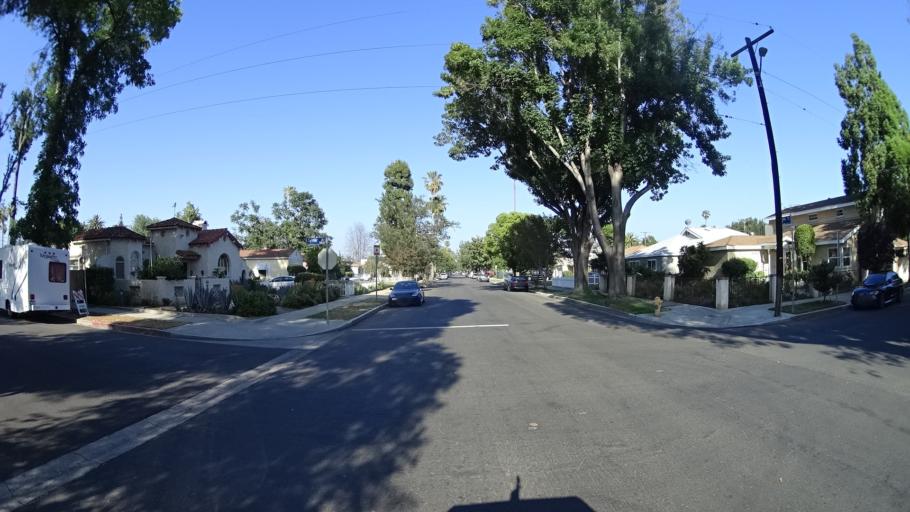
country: US
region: California
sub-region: Los Angeles County
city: Van Nuys
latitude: 34.1767
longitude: -118.4465
